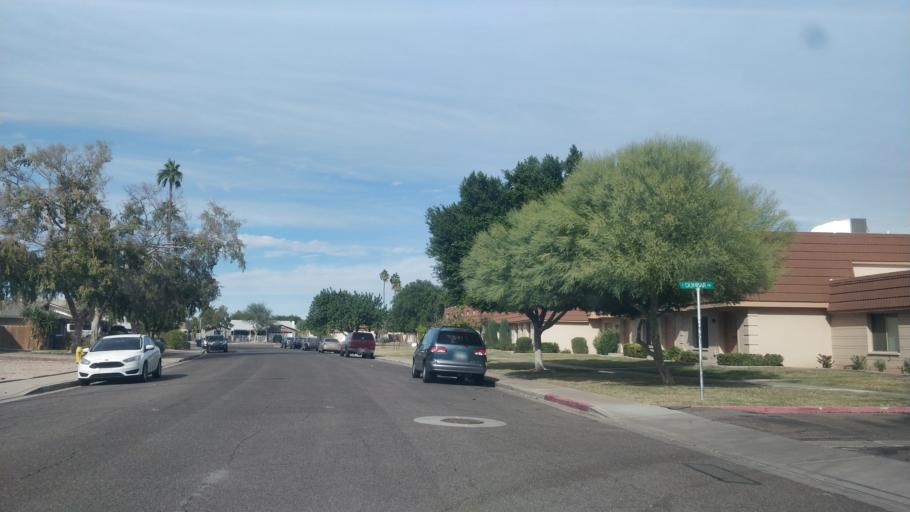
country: US
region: Arizona
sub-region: Maricopa County
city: Tempe
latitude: 33.3800
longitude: -111.9138
